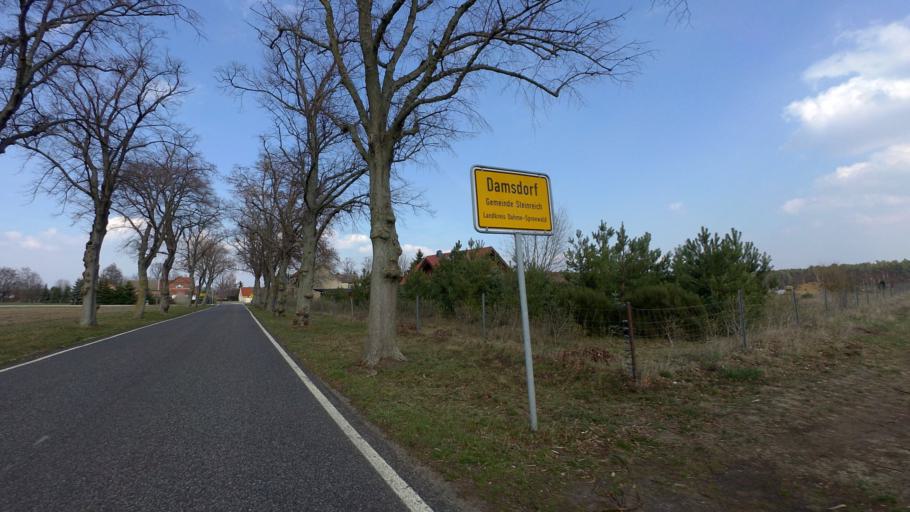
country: DE
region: Brandenburg
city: Dahme
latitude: 51.9619
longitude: 13.4359
